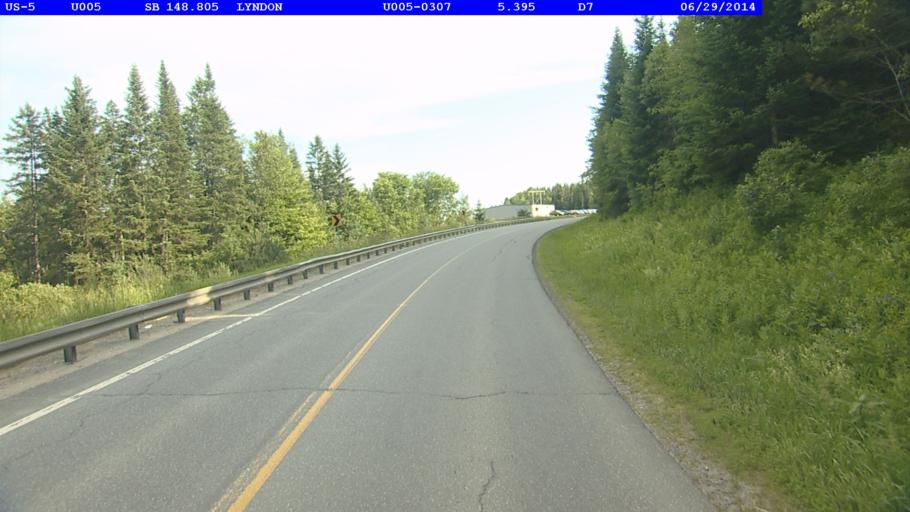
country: US
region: Vermont
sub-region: Caledonia County
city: Lyndonville
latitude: 44.5653
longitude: -71.9893
